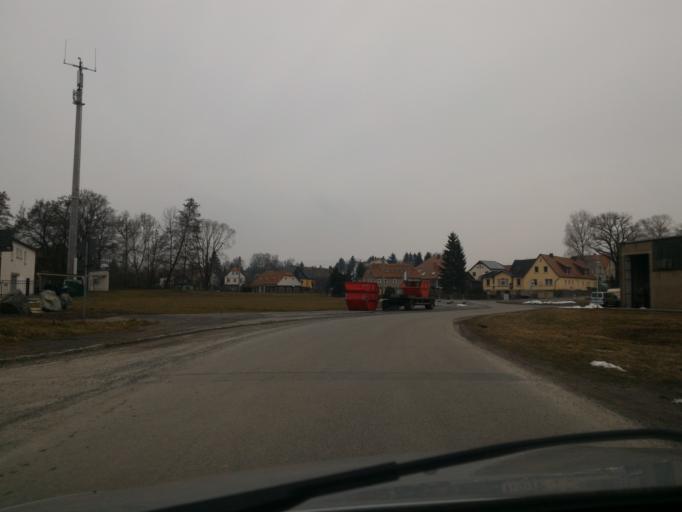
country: DE
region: Saxony
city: Leutersdorf
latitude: 50.9607
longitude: 14.6486
